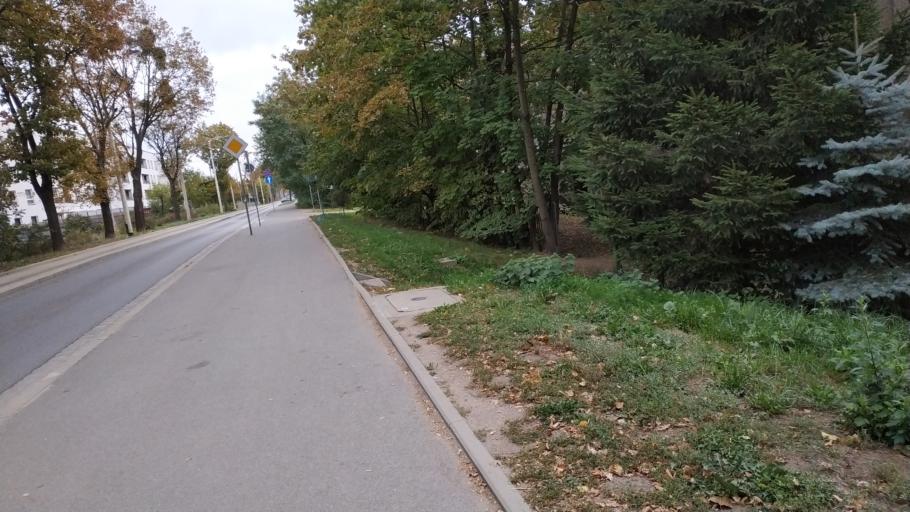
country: PL
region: Lower Silesian Voivodeship
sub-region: Powiat wroclawski
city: Bielany Wroclawskie
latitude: 51.0661
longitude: 16.9915
